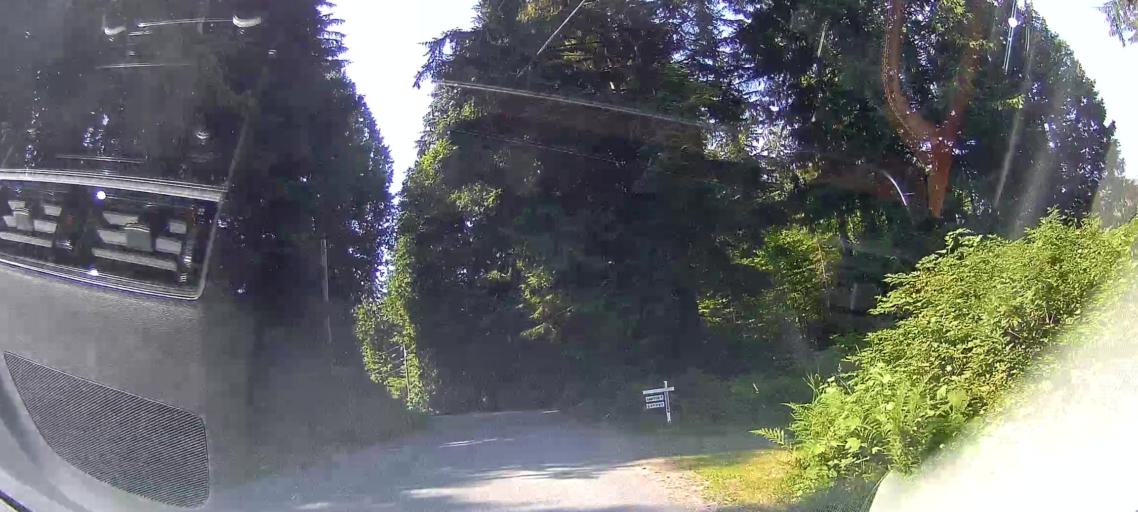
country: US
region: Washington
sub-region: Snohomish County
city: Arlington Heights
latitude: 48.3115
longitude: -121.9921
